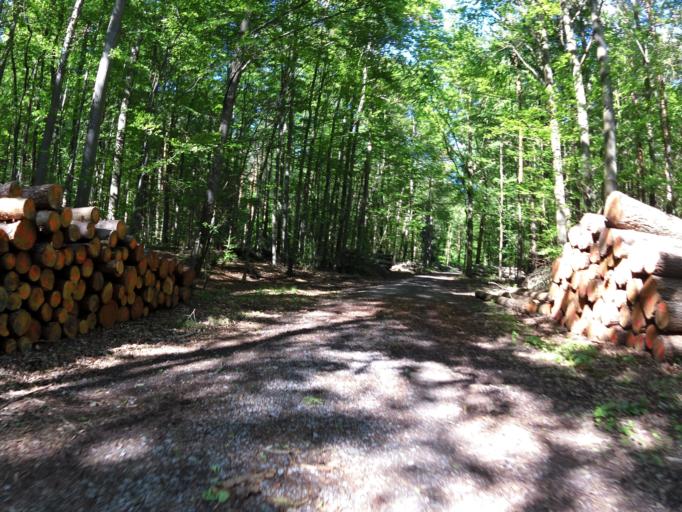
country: DE
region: Bavaria
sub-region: Regierungsbezirk Unterfranken
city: Wuerzburg
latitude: 49.7465
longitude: 9.8911
